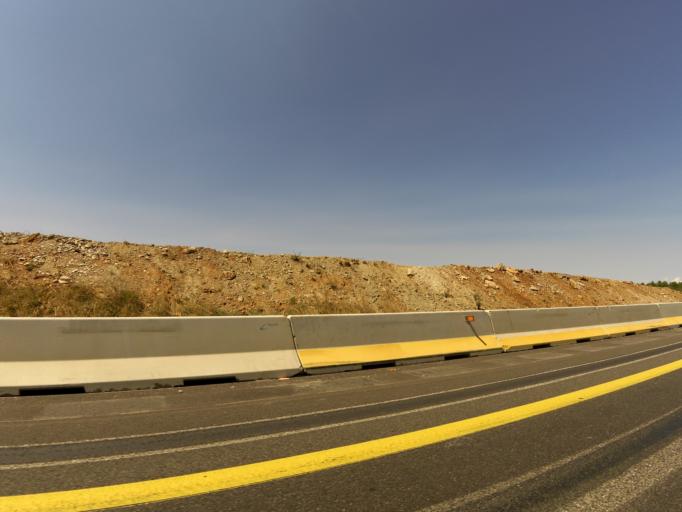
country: FR
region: Languedoc-Roussillon
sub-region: Departement de l'Herault
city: Baillargues
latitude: 43.6664
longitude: 4.0067
